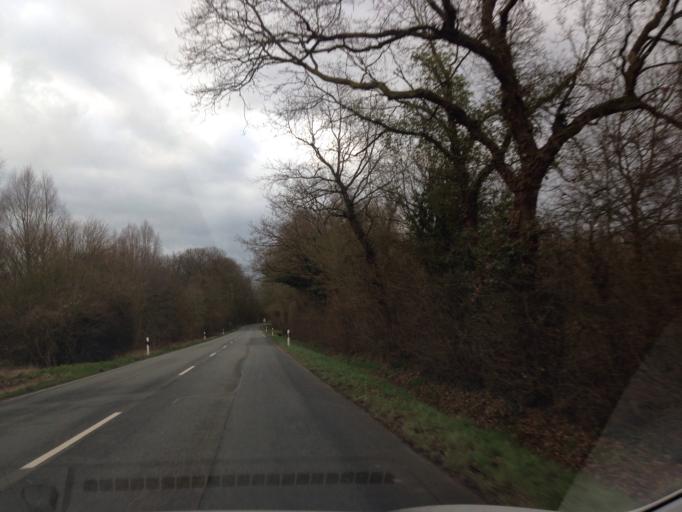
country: DE
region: North Rhine-Westphalia
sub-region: Regierungsbezirk Munster
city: Nordkirchen
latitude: 51.7546
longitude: 7.5241
